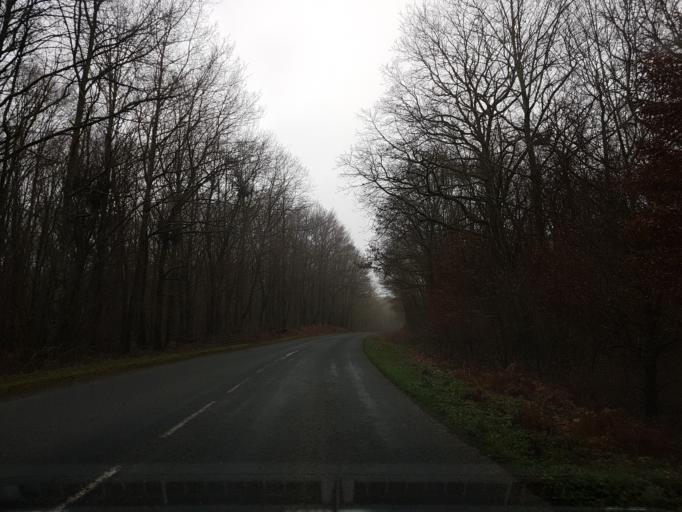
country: FR
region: Bourgogne
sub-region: Departement de Saone-et-Loire
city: Toulon-sur-Arroux
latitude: 46.6886
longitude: 4.1831
